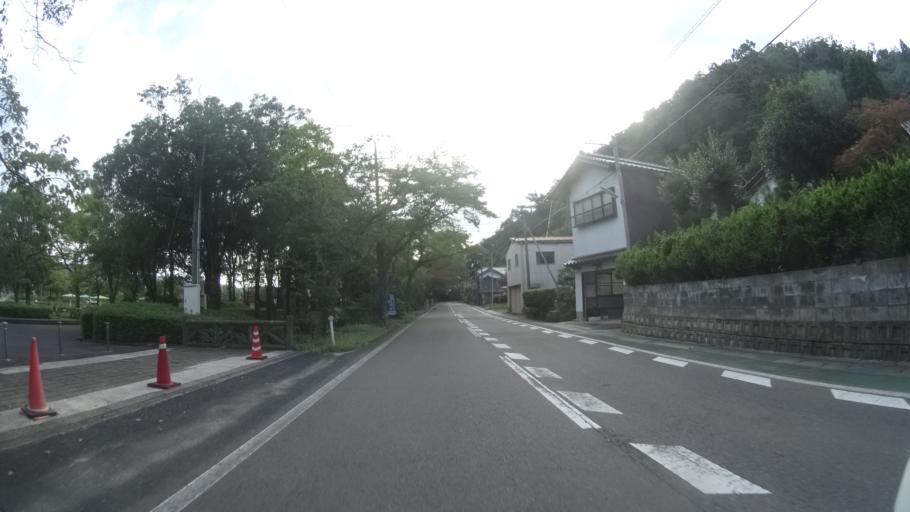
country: JP
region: Tottori
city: Kurayoshi
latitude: 35.4802
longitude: 133.9038
